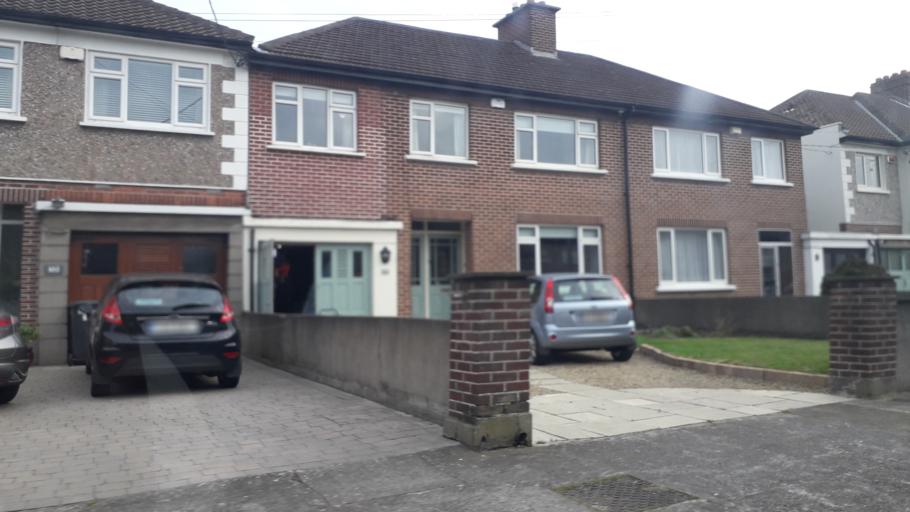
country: IE
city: Donnycarney
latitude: 53.3666
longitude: -6.2092
